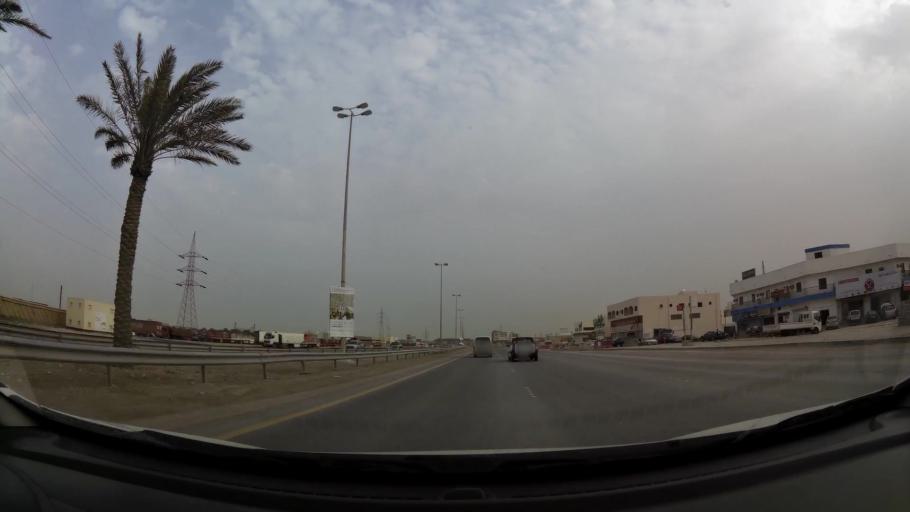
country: BH
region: Northern
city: Ar Rifa'
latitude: 26.1327
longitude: 50.5855
